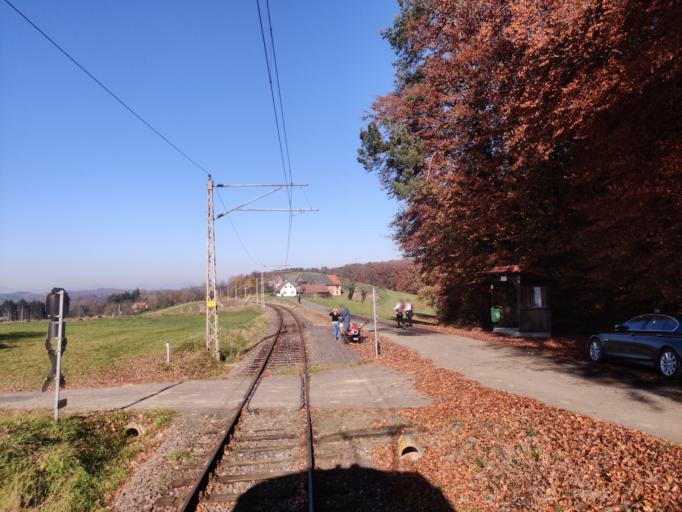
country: AT
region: Styria
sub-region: Politischer Bezirk Suedoststeiermark
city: Maierdorf
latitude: 46.8946
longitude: 15.8343
